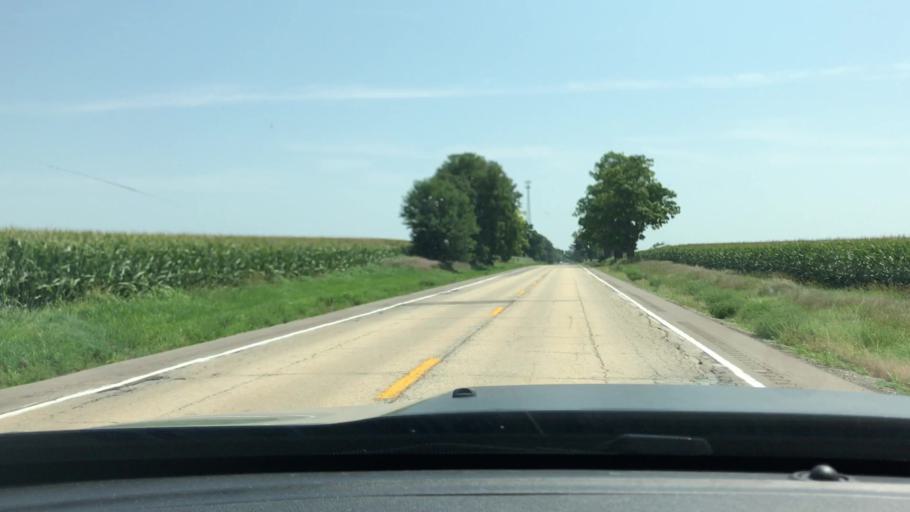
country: US
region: Illinois
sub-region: LaSalle County
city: Earlville
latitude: 41.4690
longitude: -88.9465
